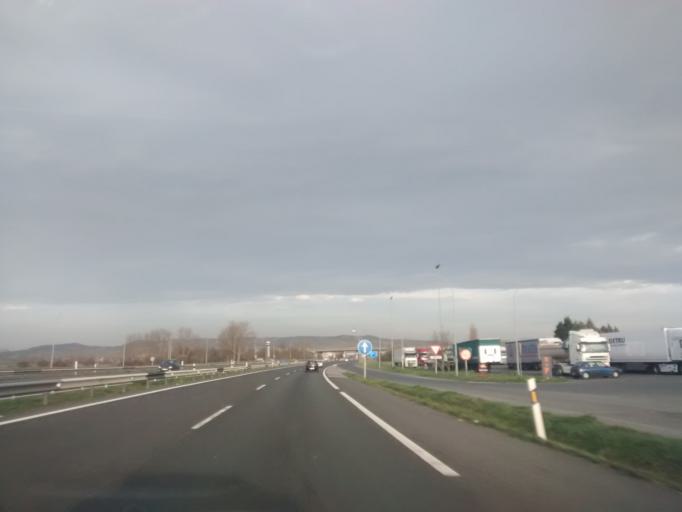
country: ES
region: Basque Country
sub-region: Provincia de Alava
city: Gasteiz / Vitoria
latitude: 42.8777
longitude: -2.7131
